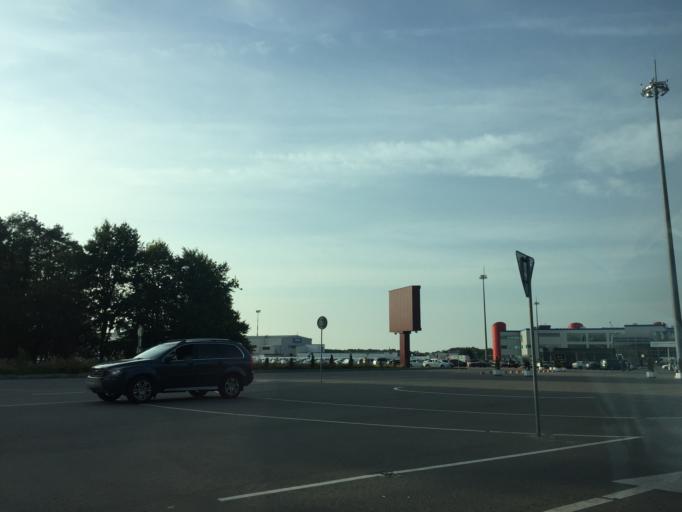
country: RU
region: Kaliningrad
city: Gur'yevsk
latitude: 54.8807
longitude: 20.5870
